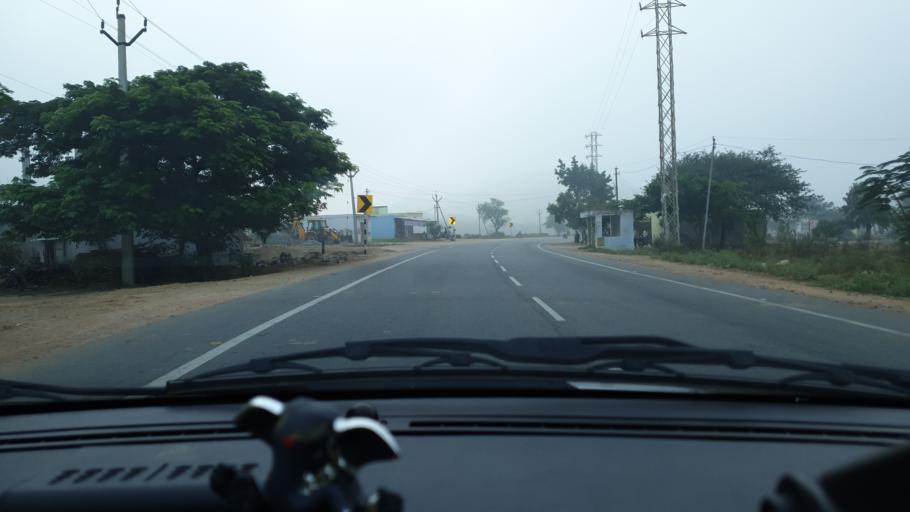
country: IN
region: Telangana
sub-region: Mahbubnagar
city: Farrukhnagar
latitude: 16.9023
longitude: 78.5306
